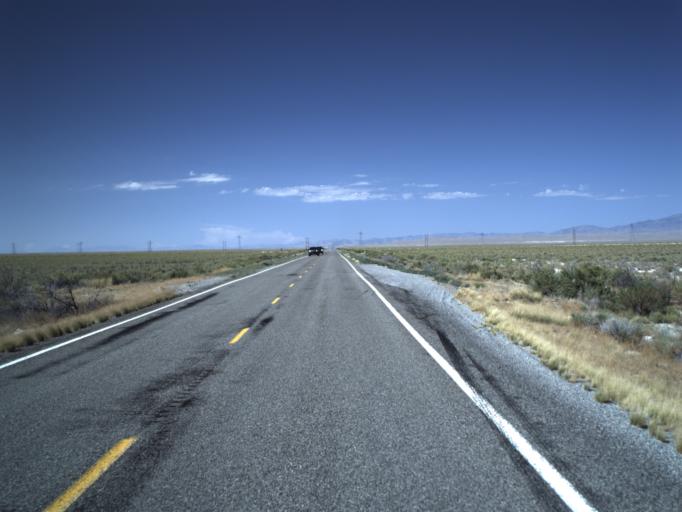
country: US
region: Utah
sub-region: Millard County
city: Delta
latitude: 39.2590
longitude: -112.8826
